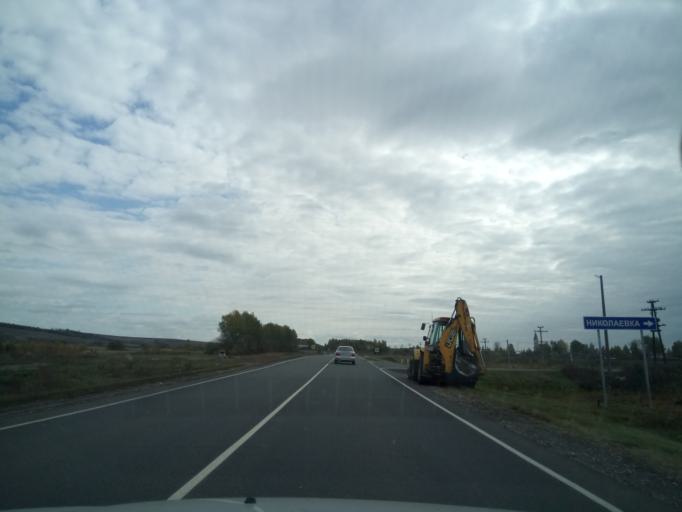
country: RU
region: Nizjnij Novgorod
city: Lukoyanov
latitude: 55.0689
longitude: 44.3441
